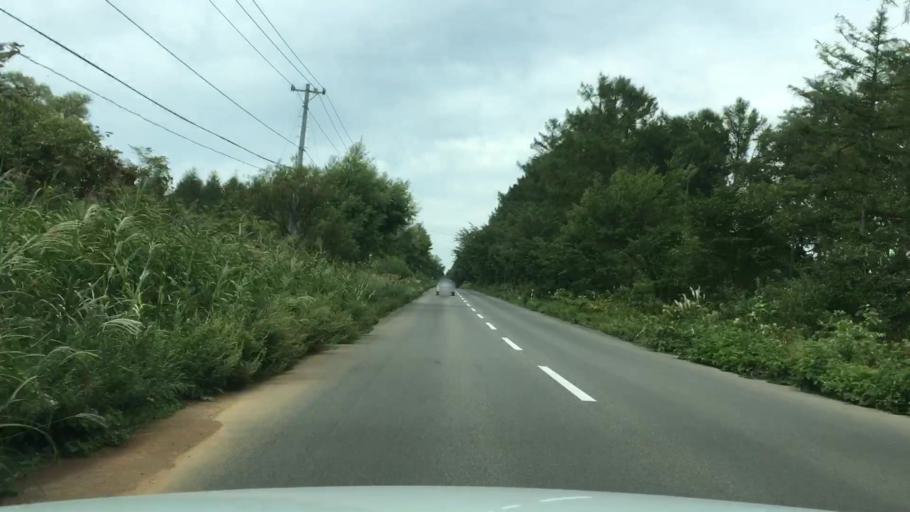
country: JP
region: Aomori
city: Shimokizukuri
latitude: 40.7131
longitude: 140.3242
